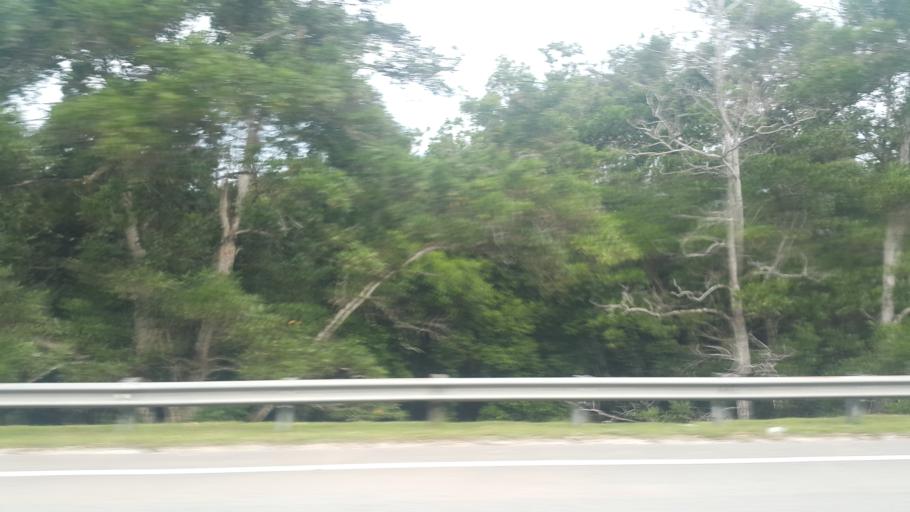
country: MY
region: Johor
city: Skudai
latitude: 1.4343
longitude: 103.6066
